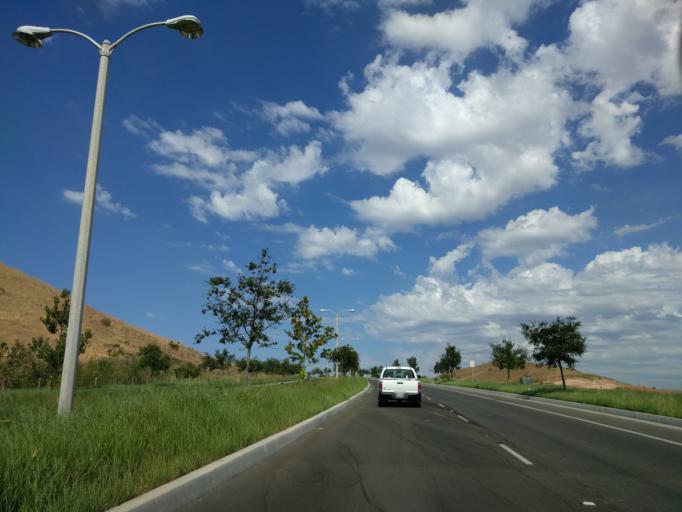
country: US
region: California
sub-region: Orange County
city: Laguna Woods
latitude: 33.6341
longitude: -117.7481
